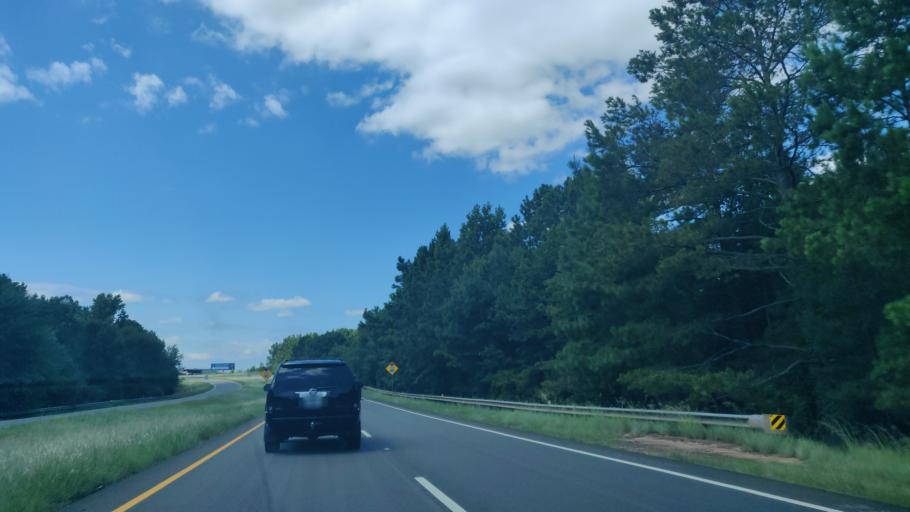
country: US
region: Georgia
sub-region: Stewart County
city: Richland
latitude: 32.0943
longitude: -84.6750
